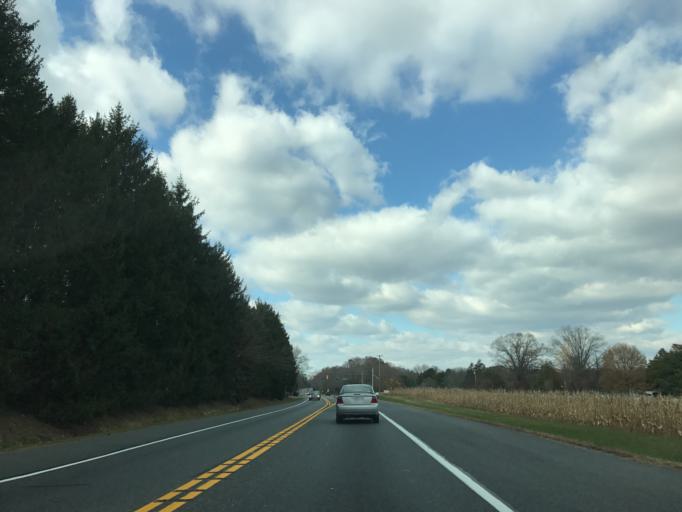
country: US
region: Maryland
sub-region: Harford County
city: Pleasant Hills
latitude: 39.4748
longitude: -76.3779
